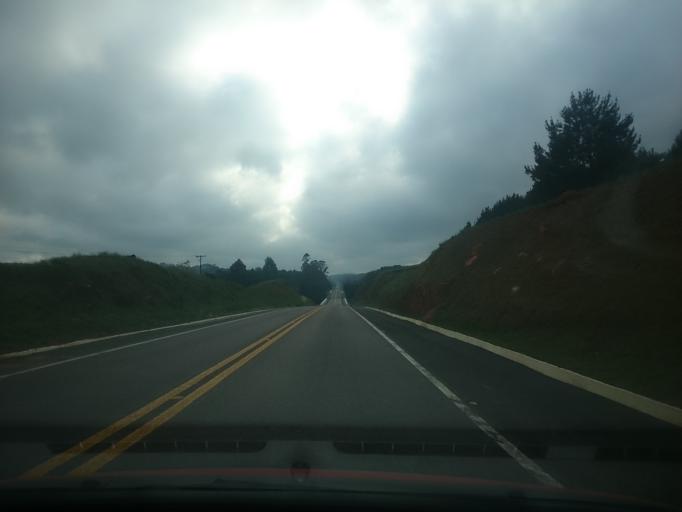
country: BR
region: Santa Catarina
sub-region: Lages
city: Lages
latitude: -27.8775
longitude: -50.4058
